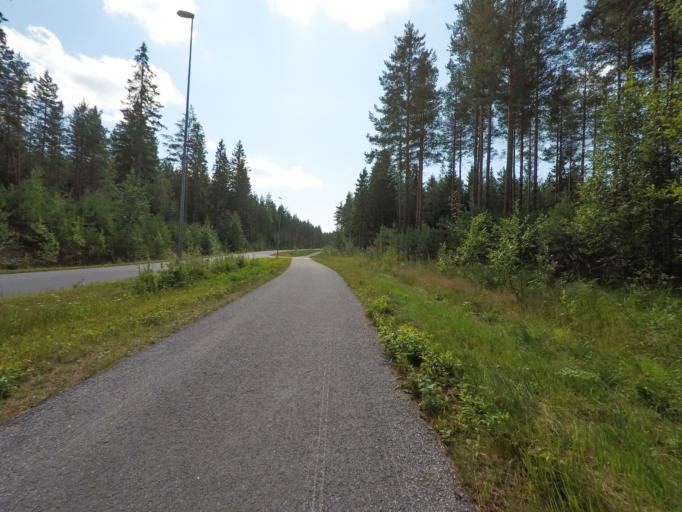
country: FI
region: Southern Savonia
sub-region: Mikkeli
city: Puumala
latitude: 61.5130
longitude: 28.1640
